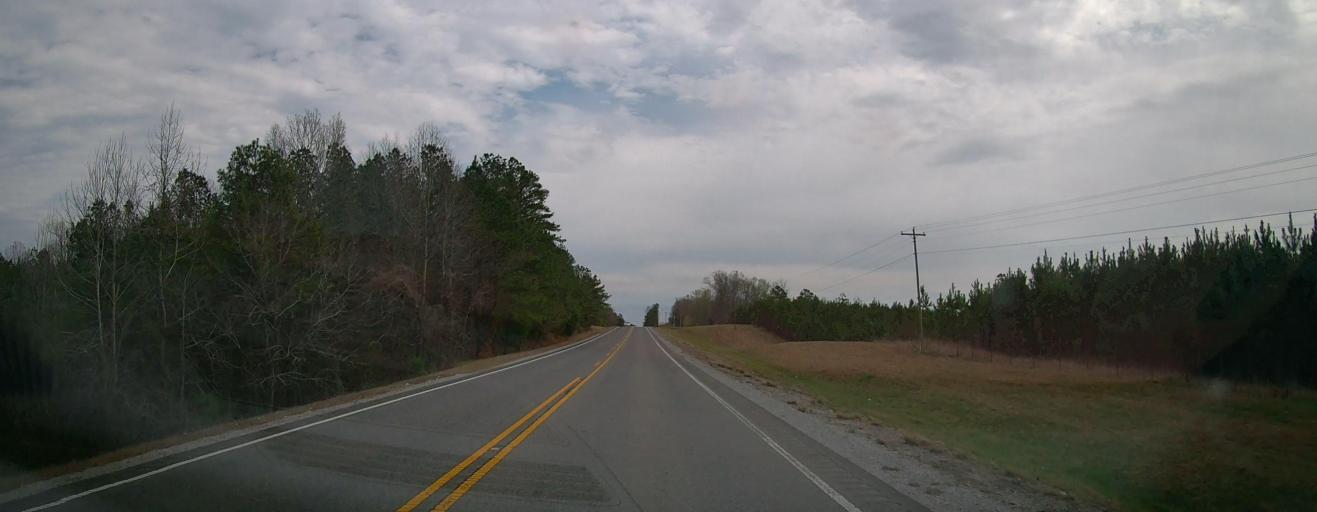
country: US
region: Alabama
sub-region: Marion County
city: Guin
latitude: 34.0369
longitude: -87.9494
